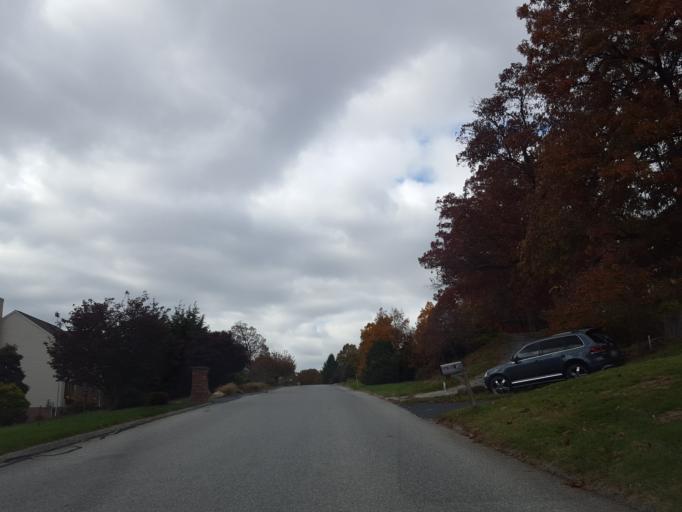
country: US
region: Pennsylvania
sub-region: York County
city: Red Lion
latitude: 39.9114
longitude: -76.6132
